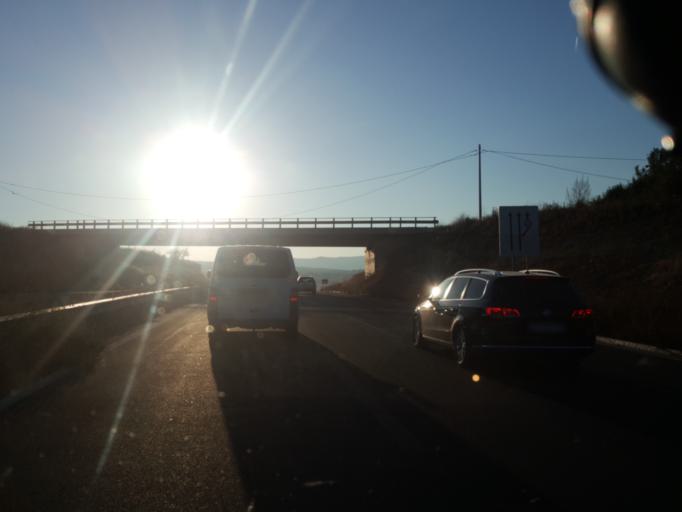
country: XK
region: Prizren
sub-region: Komuna e Malisheves
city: Llazice
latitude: 42.5754
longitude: 20.7210
